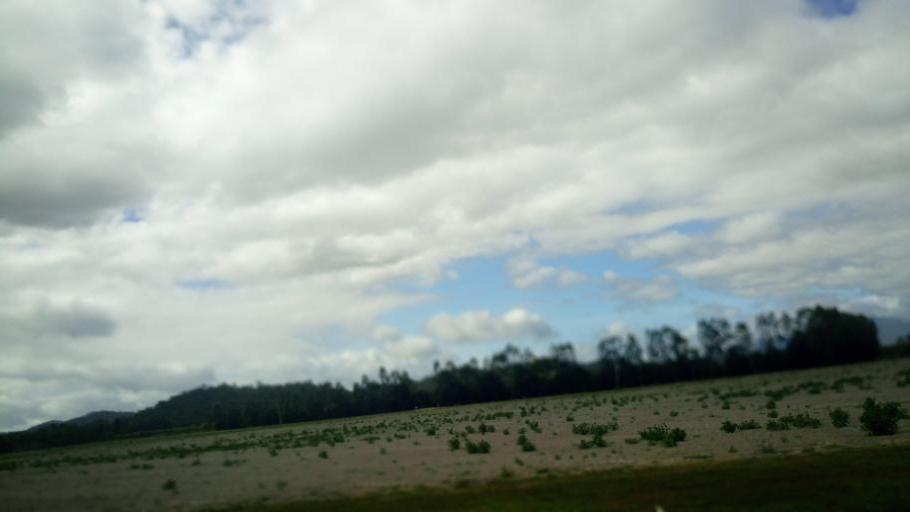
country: AU
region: Queensland
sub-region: Tablelands
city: Mareeba
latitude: -16.9711
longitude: 145.4569
